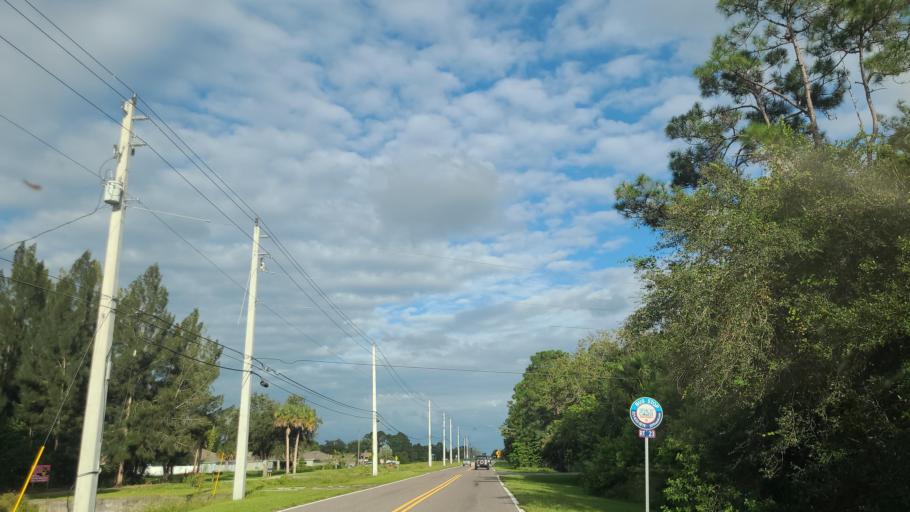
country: US
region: Florida
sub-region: Brevard County
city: June Park
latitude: 27.9991
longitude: -80.6917
